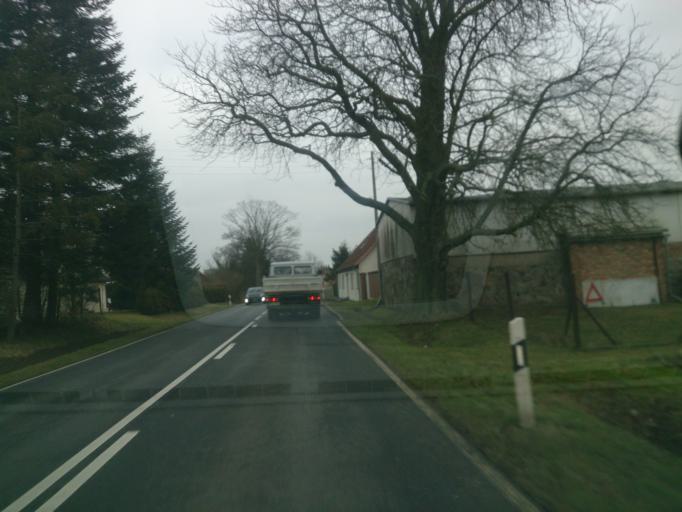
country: DE
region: Mecklenburg-Vorpommern
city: Borrentin
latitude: 53.8213
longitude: 12.9777
